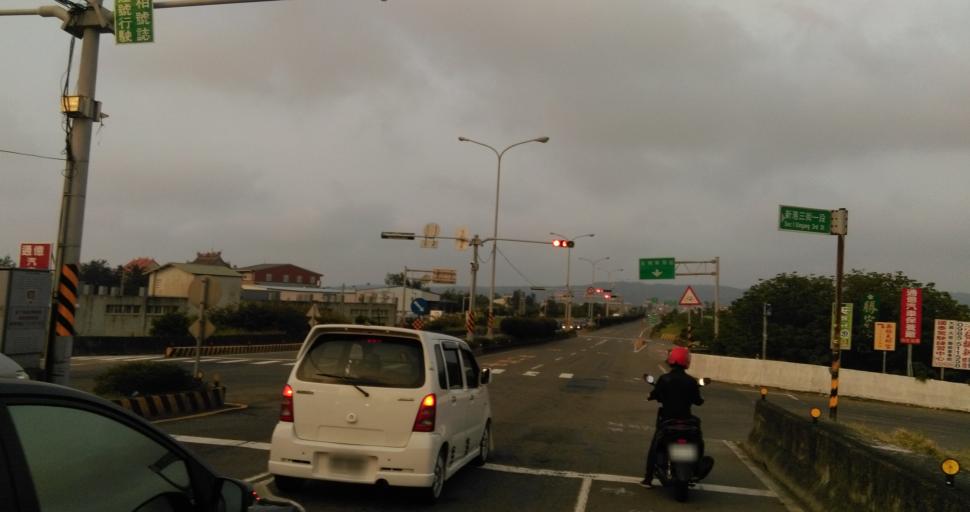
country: TW
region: Taiwan
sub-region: Hsinchu
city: Hsinchu
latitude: 24.8519
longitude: 120.9428
